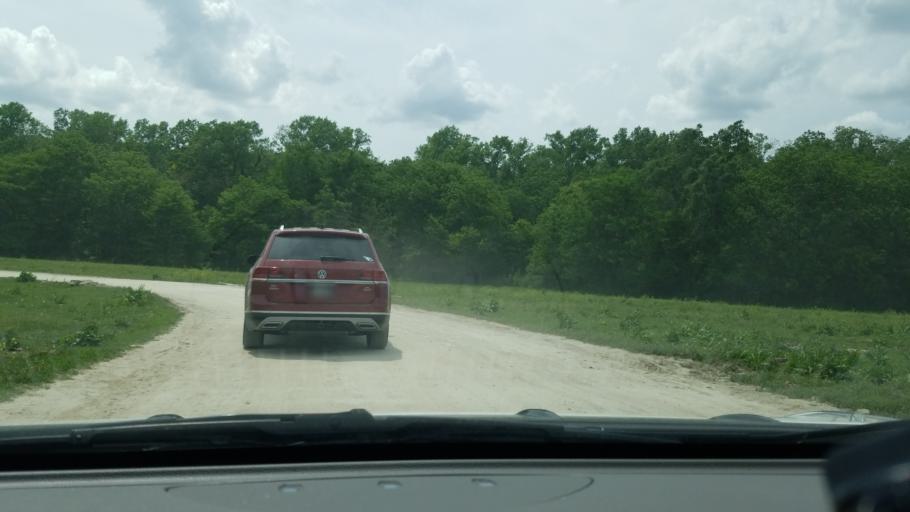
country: US
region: Nebraska
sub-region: Saunders County
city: Ashland
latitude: 41.0167
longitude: -96.2950
